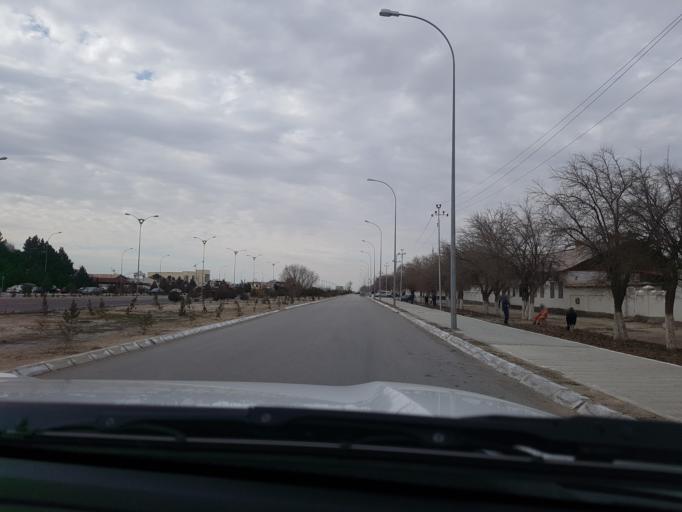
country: TM
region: Balkan
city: Balkanabat
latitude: 39.4976
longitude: 54.3716
